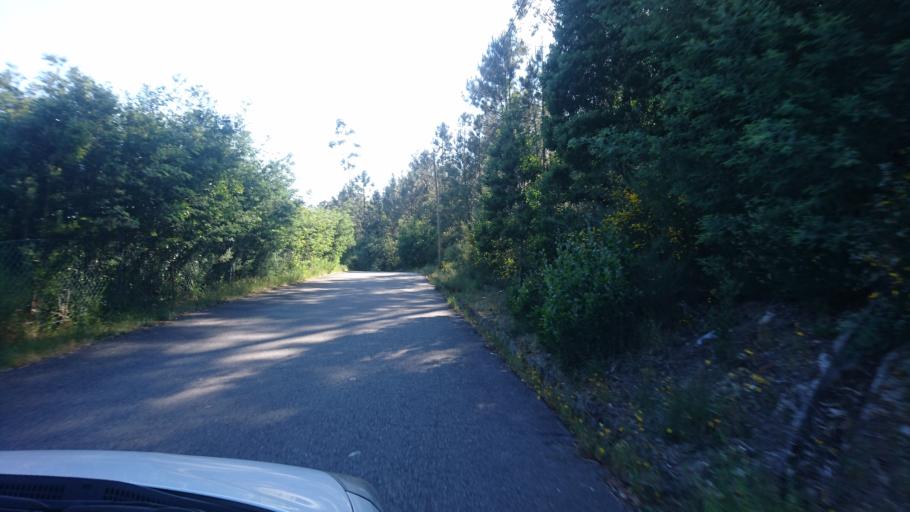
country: PT
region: Porto
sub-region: Paredes
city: Recarei
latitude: 41.1567
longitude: -8.3825
